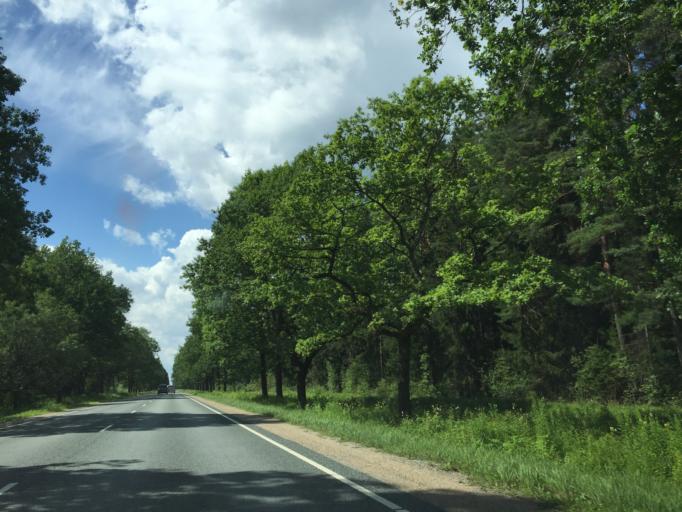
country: LV
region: Ozolnieku
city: Ozolnieki
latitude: 56.7062
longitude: 23.8206
